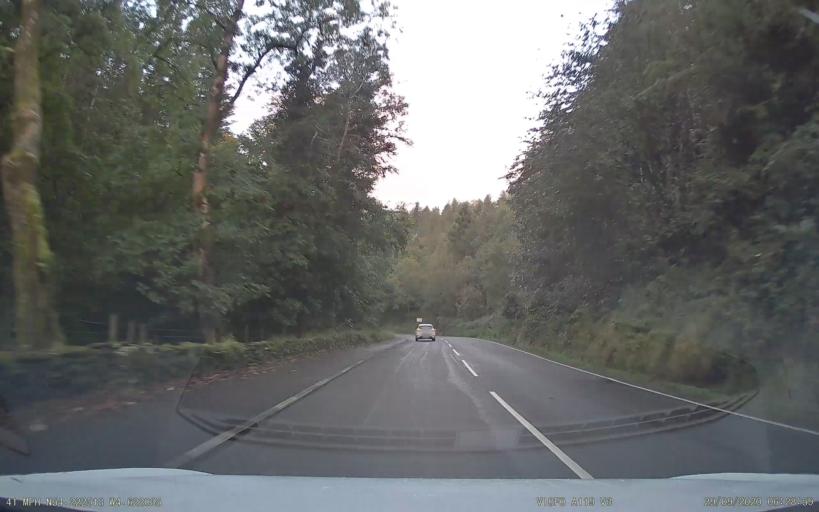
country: IM
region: Castletown
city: Castletown
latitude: 54.2225
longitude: -4.6220
